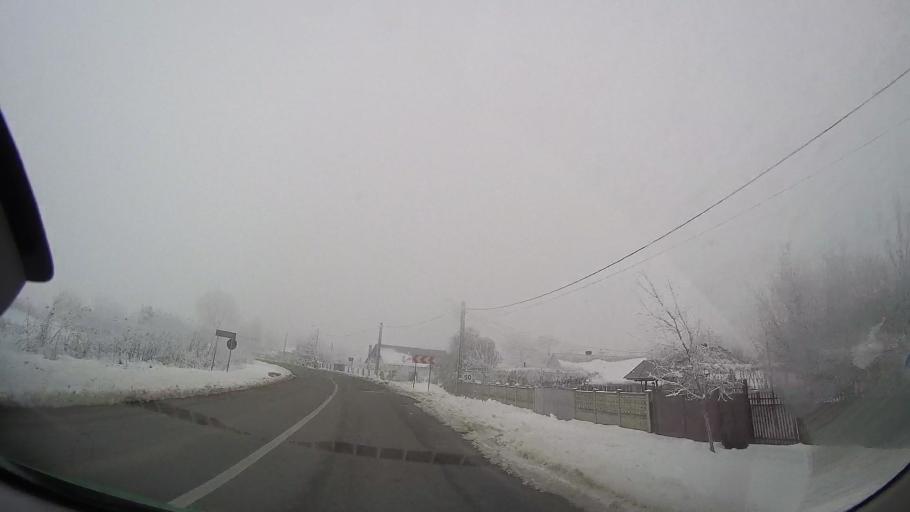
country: RO
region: Iasi
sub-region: Comuna Mogosesti-Siret
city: Mogosesti-Siret
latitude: 47.1573
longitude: 26.7763
